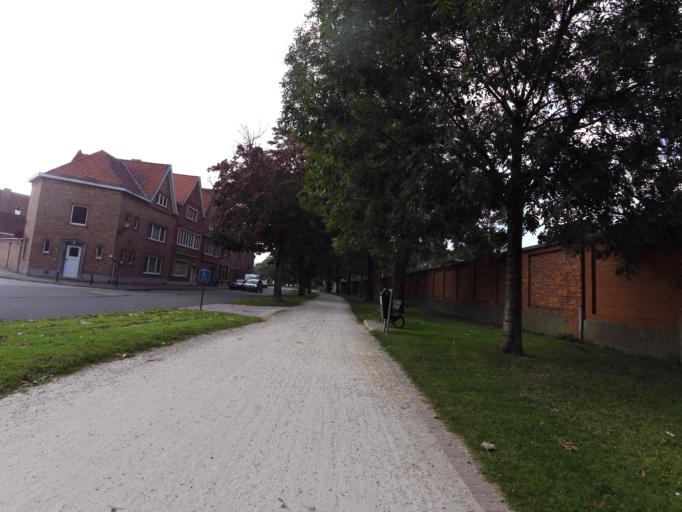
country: BE
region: Flanders
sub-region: Provincie West-Vlaanderen
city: Brugge
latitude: 51.2210
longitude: 3.2283
